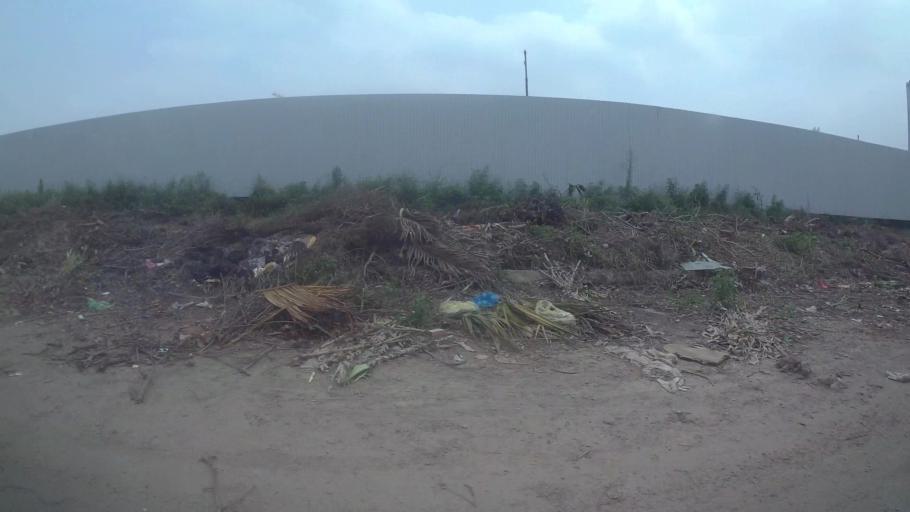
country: VN
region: Ha Noi
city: Tay Ho
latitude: 21.0856
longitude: 105.7963
